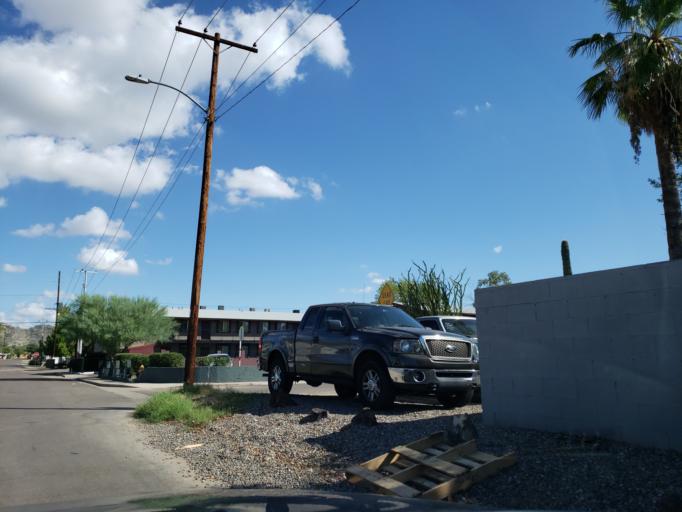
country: US
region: Arizona
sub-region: Maricopa County
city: Phoenix
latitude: 33.5721
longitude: -112.0631
